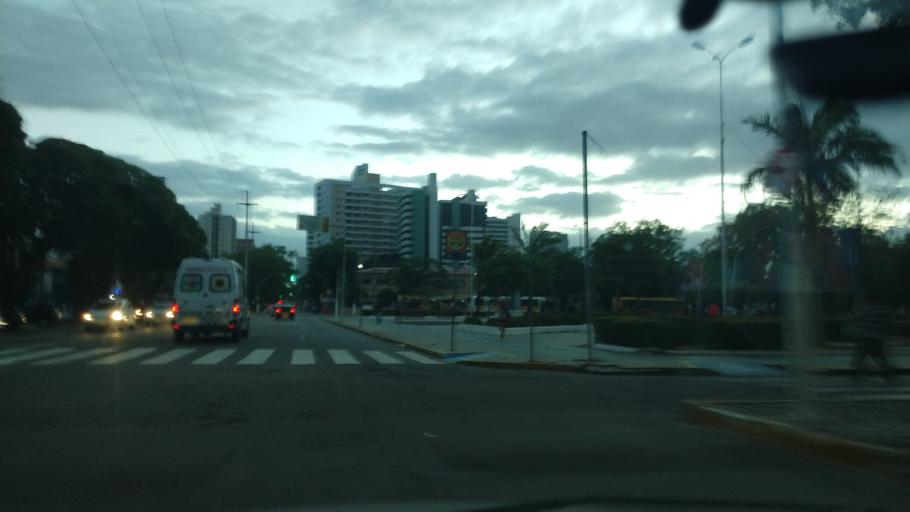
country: BR
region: Rio Grande do Norte
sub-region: Natal
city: Natal
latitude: -5.7841
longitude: -35.2000
